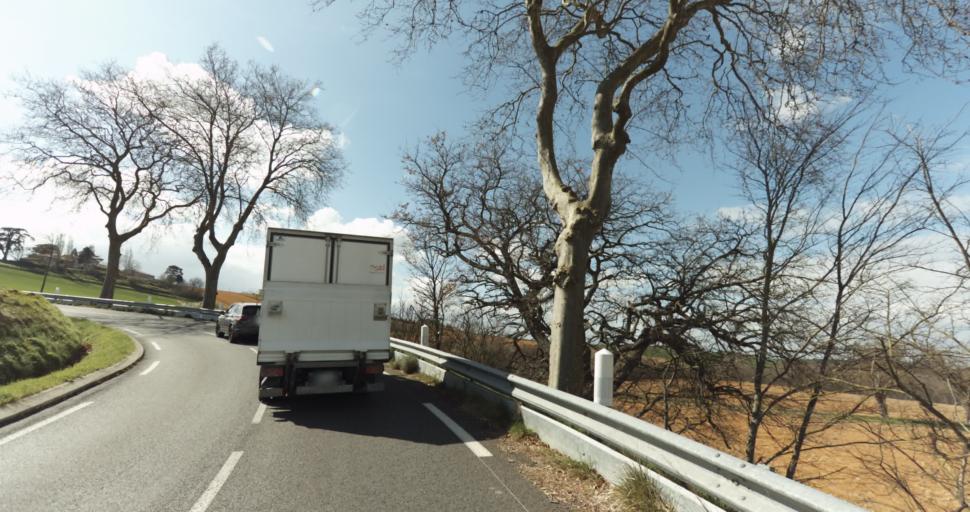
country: FR
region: Midi-Pyrenees
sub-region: Departement de la Haute-Garonne
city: Auterive
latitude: 43.3587
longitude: 1.5219
